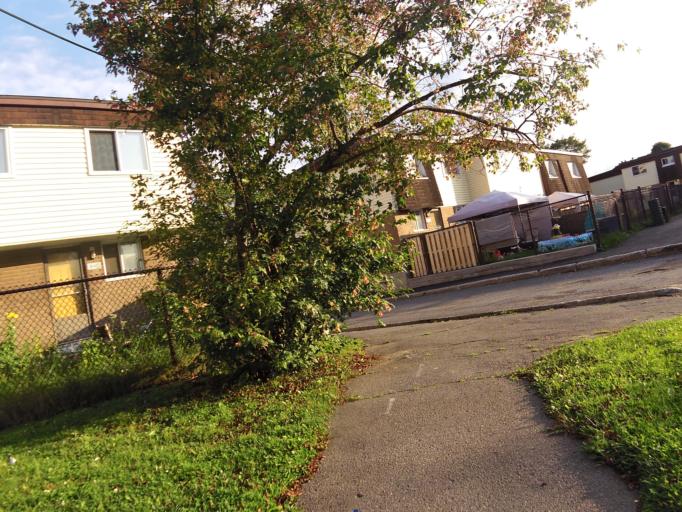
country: CA
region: Ontario
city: Ottawa
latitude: 45.3682
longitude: -75.7047
